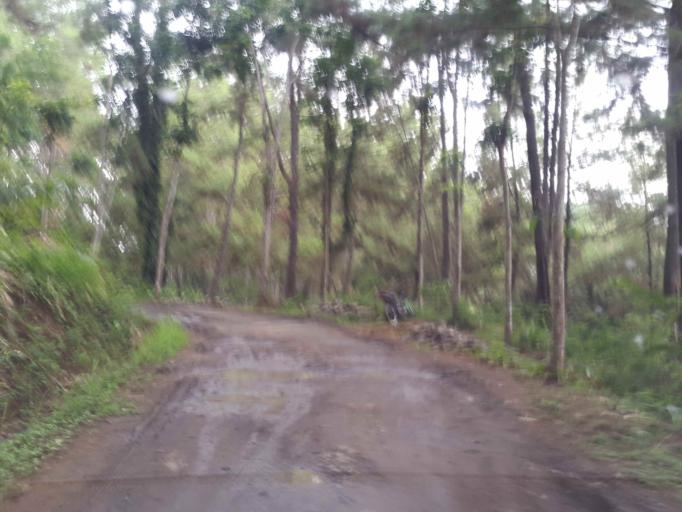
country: ID
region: Central Java
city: Genteng Wetan
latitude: -7.3546
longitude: 108.9132
